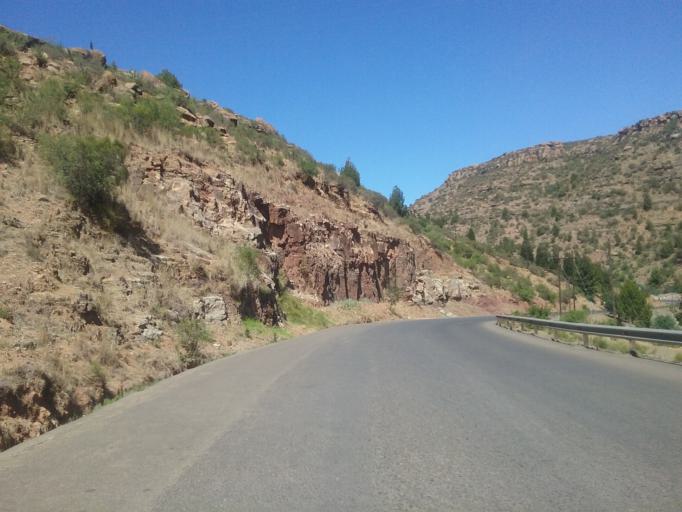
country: LS
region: Quthing
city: Quthing
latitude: -30.3990
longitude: 27.6898
